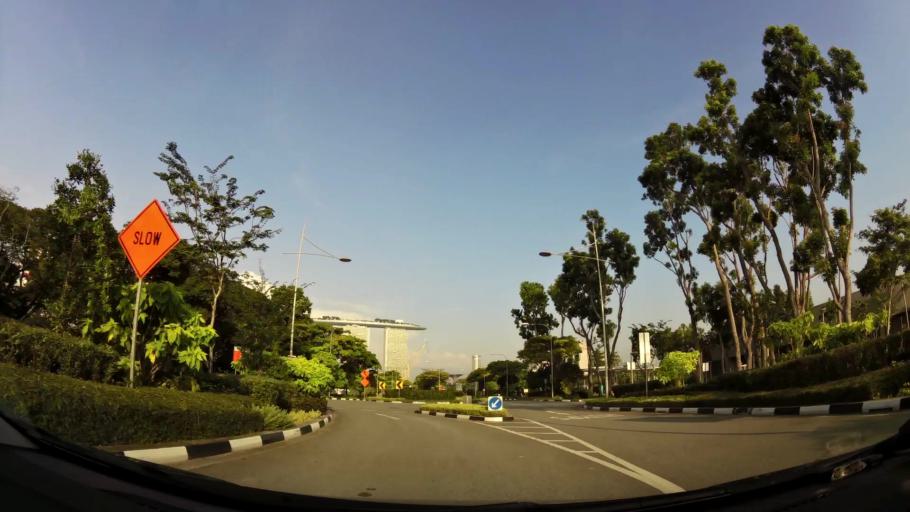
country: SG
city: Singapore
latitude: 1.2790
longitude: 103.8705
